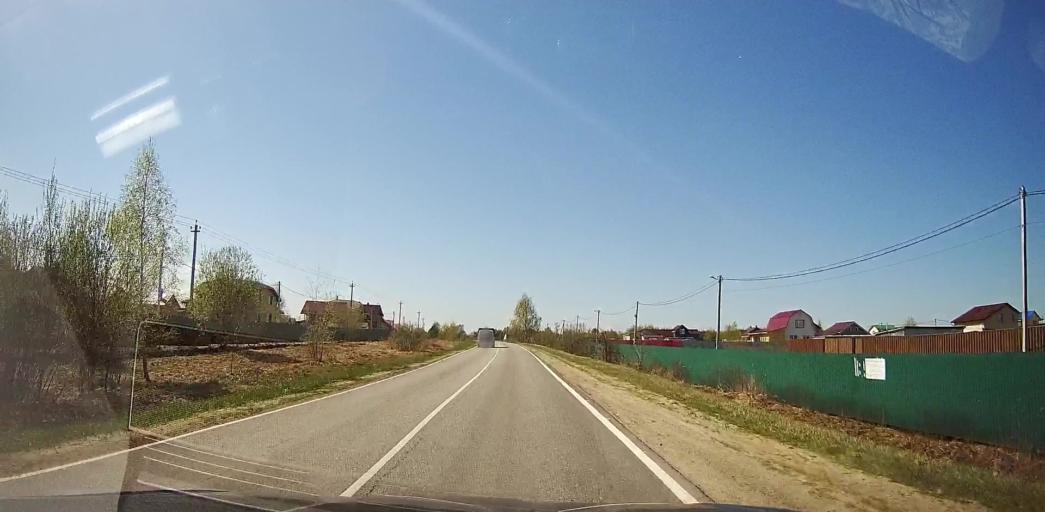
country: RU
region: Moskovskaya
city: Bronnitsy
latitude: 55.4565
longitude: 38.2841
